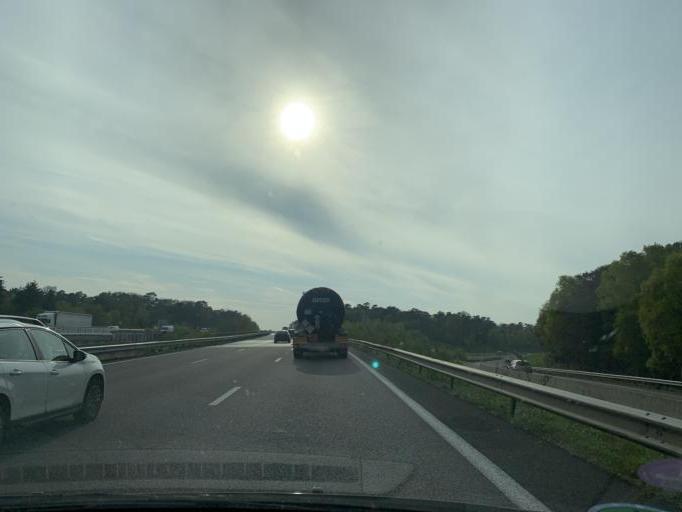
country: FR
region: Haute-Normandie
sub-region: Departement de la Seine-Maritime
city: Cleon
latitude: 49.3443
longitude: 1.0458
